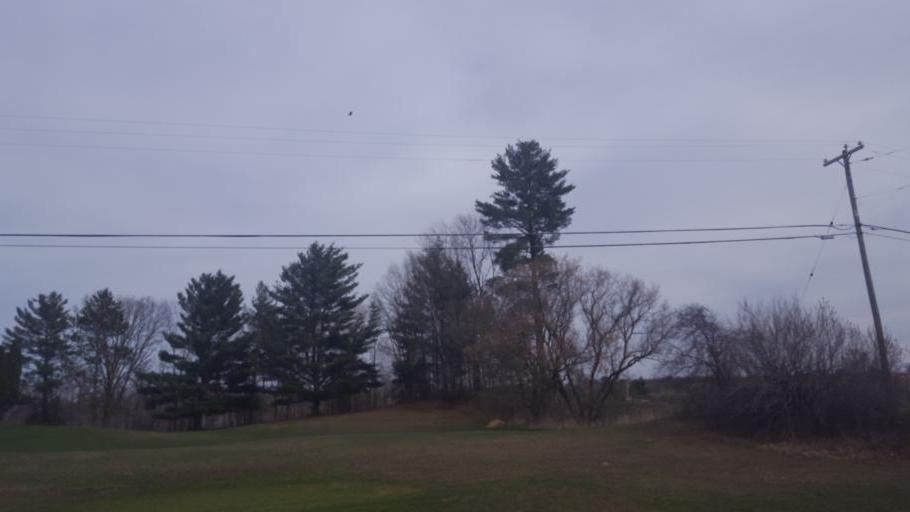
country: US
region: Michigan
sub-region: Clare County
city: Clare
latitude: 43.8512
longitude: -84.7681
